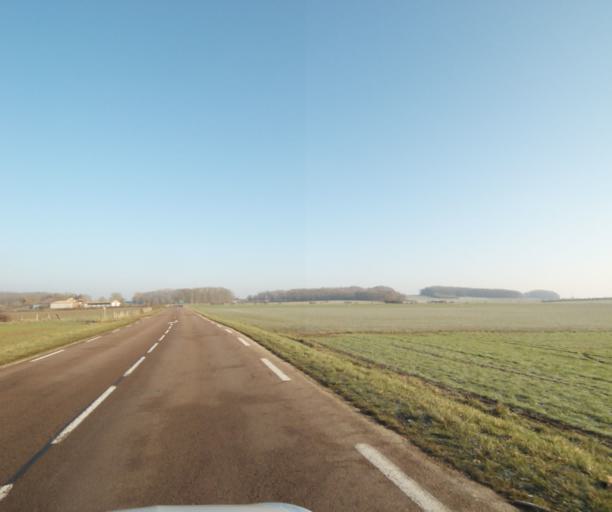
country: FR
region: Champagne-Ardenne
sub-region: Departement de la Haute-Marne
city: Montier-en-Der
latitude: 48.4447
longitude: 4.7344
